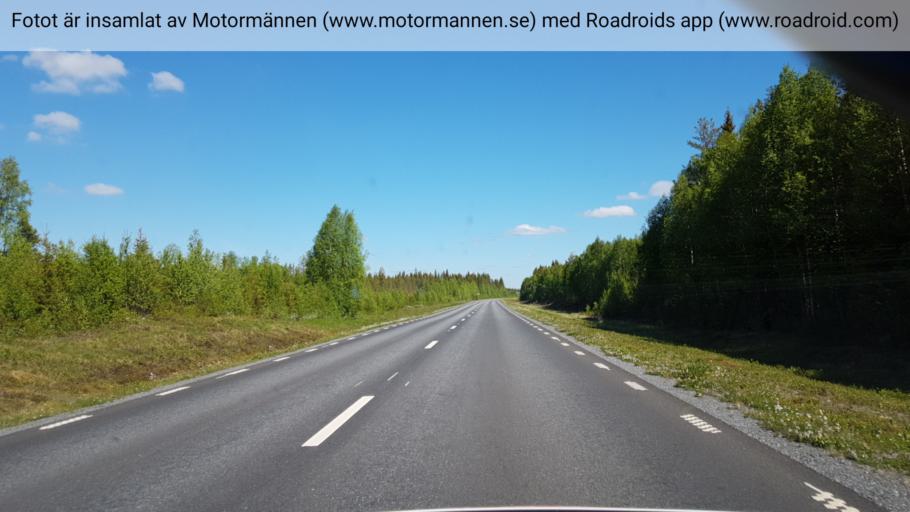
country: SE
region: Vaesterbotten
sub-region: Vilhelmina Kommun
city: Vilhelmina
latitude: 64.3715
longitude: 16.7104
